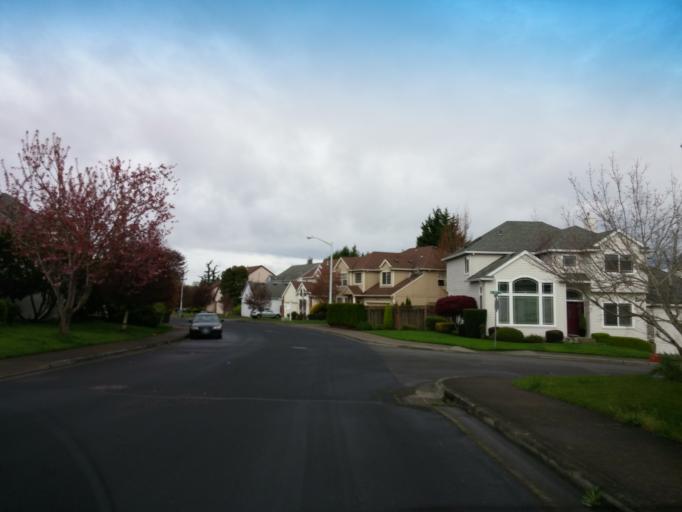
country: US
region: Oregon
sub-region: Washington County
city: Oak Hills
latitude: 45.5389
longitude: -122.8473
